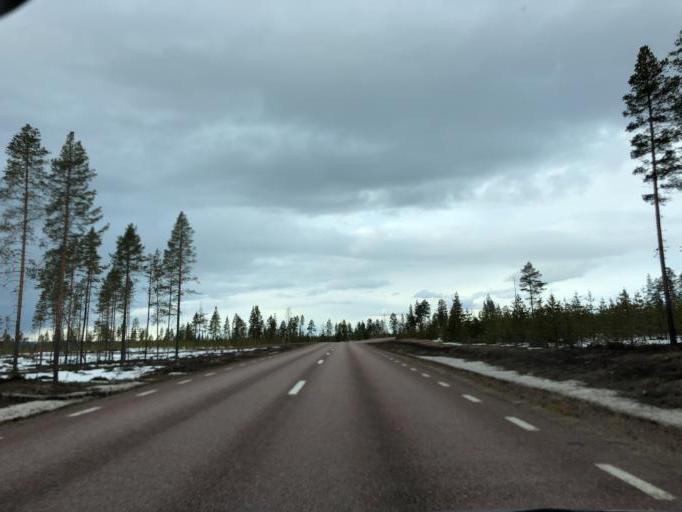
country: SE
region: Dalarna
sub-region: Alvdalens Kommun
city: AElvdalen
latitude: 61.4643
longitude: 13.4260
